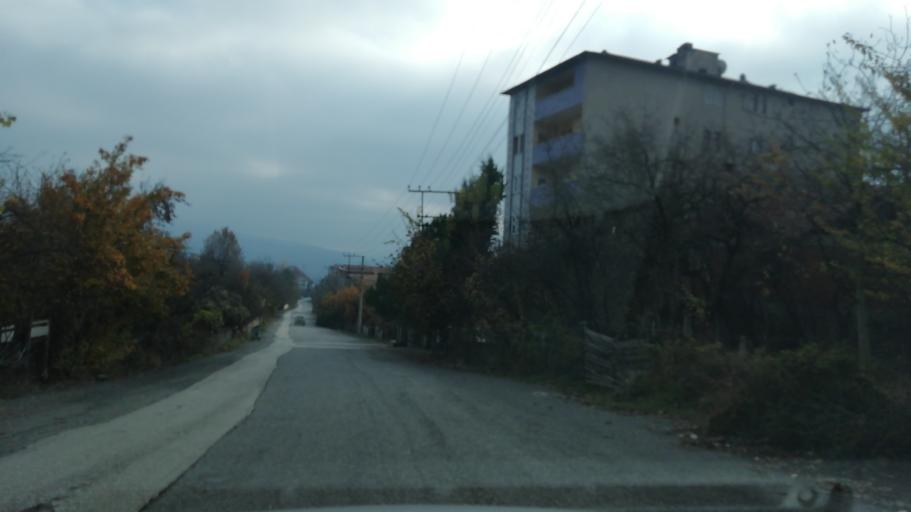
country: TR
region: Karabuk
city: Karabuk
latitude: 41.2255
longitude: 32.6232
